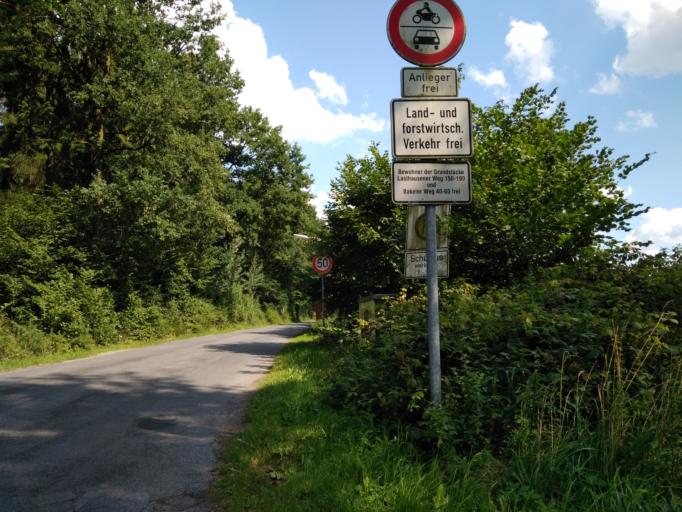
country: DE
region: North Rhine-Westphalia
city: Dorsten
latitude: 51.7339
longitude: 6.9734
